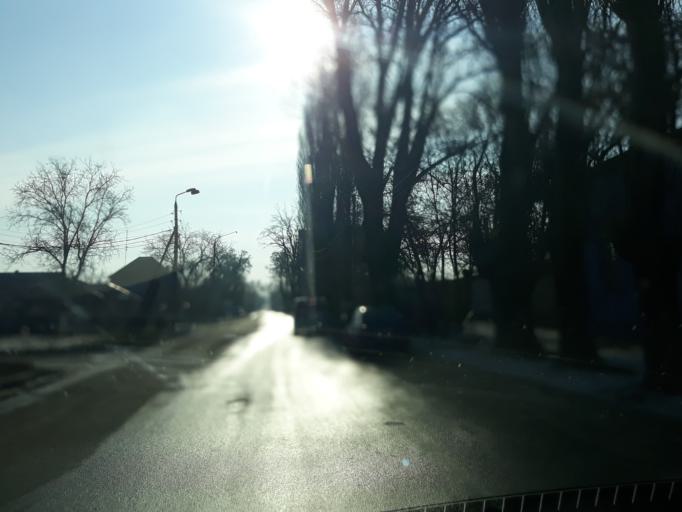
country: RU
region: Rostov
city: Taganrog
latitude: 47.2254
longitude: 38.9096
